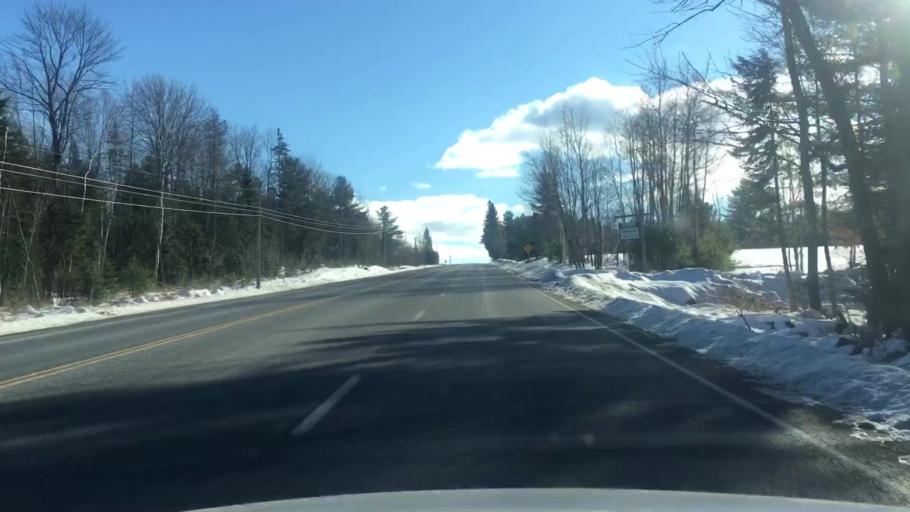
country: US
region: Maine
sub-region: Somerset County
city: Madison
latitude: 44.8964
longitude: -69.8095
